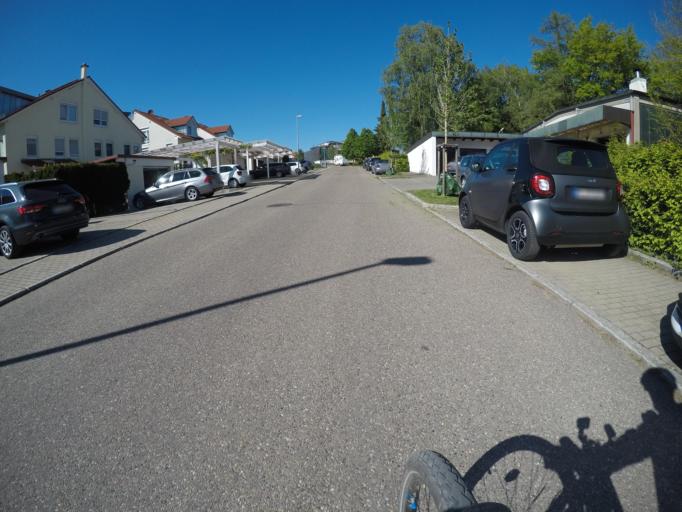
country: DE
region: Baden-Wuerttemberg
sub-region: Karlsruhe Region
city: Friolzheim
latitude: 48.8328
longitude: 8.8402
